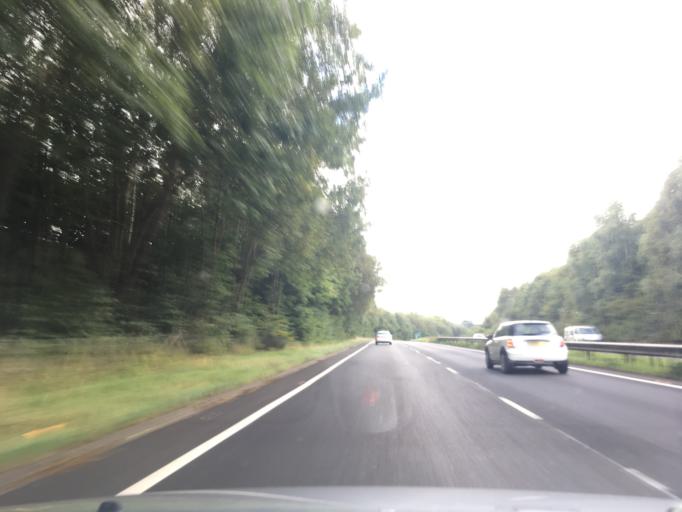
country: GB
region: England
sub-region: Hampshire
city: Liphook
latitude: 51.0840
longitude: -0.8106
